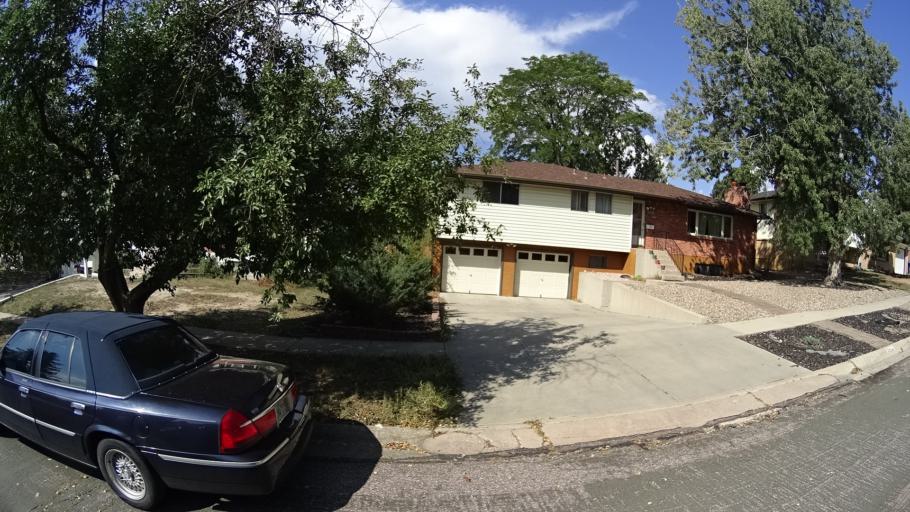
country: US
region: Colorado
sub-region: El Paso County
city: Colorado Springs
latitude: 38.8648
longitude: -104.7640
